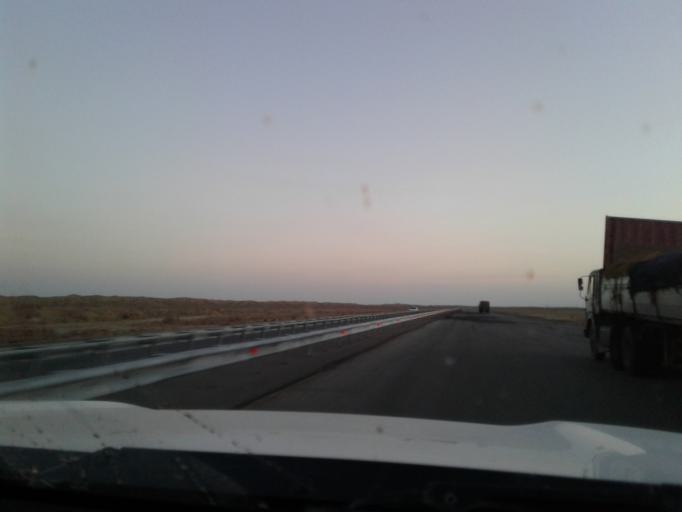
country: TM
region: Ahal
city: Abadan
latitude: 38.5554
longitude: 58.5094
